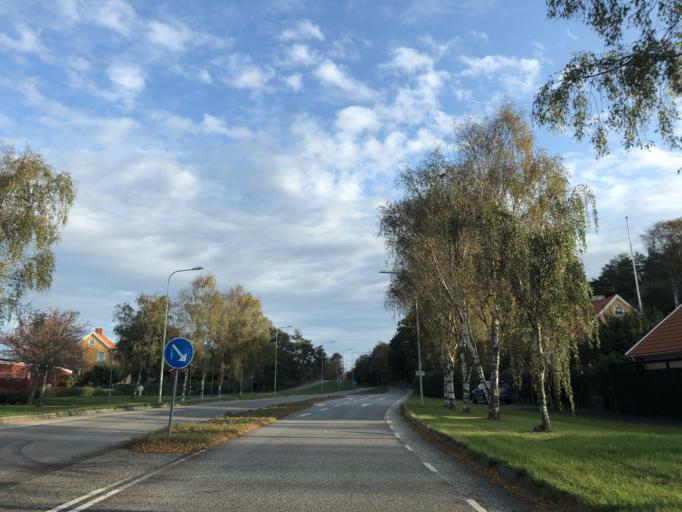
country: SE
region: Vaestra Goetaland
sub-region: Goteborg
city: Majorna
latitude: 57.6567
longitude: 11.8704
